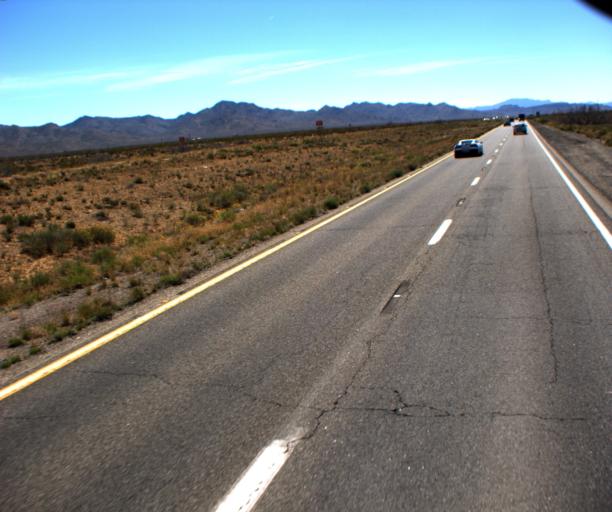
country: US
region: Arizona
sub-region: Mohave County
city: Golden Valley
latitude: 35.3312
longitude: -114.2121
